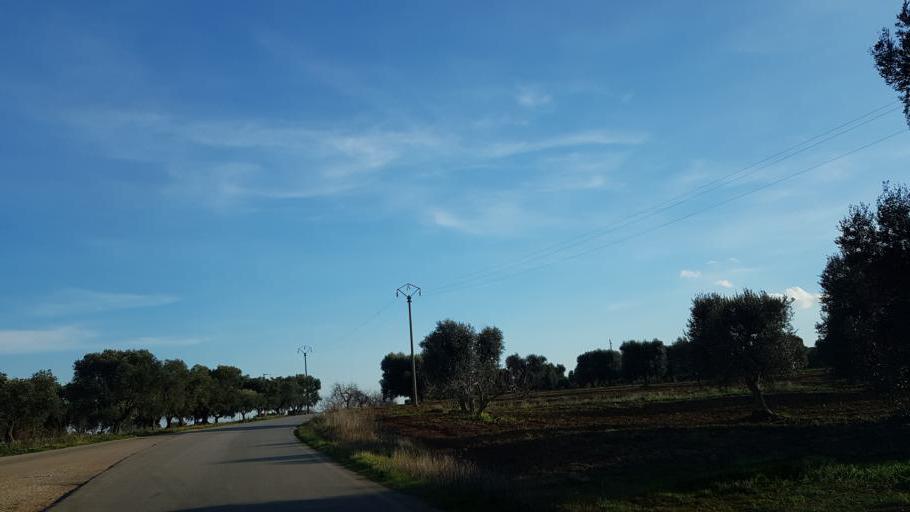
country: IT
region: Apulia
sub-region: Provincia di Brindisi
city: San Vito dei Normanni
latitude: 40.6898
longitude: 17.7638
